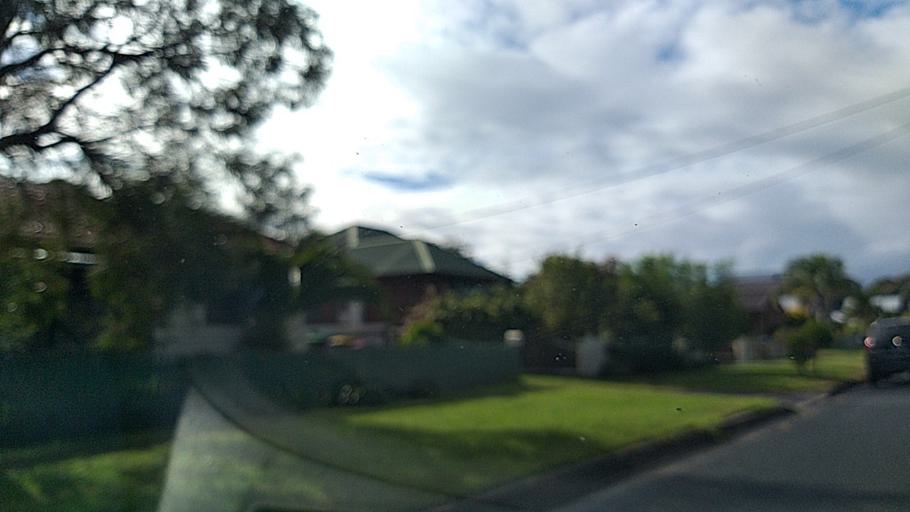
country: AU
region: New South Wales
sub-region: Wollongong
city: East Corrimal
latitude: -34.3755
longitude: 150.9126
